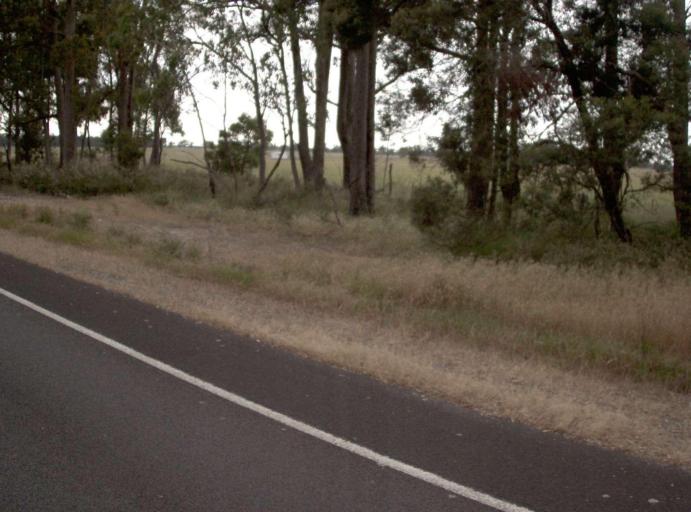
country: AU
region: Victoria
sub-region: Wellington
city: Sale
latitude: -38.4592
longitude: 146.9357
